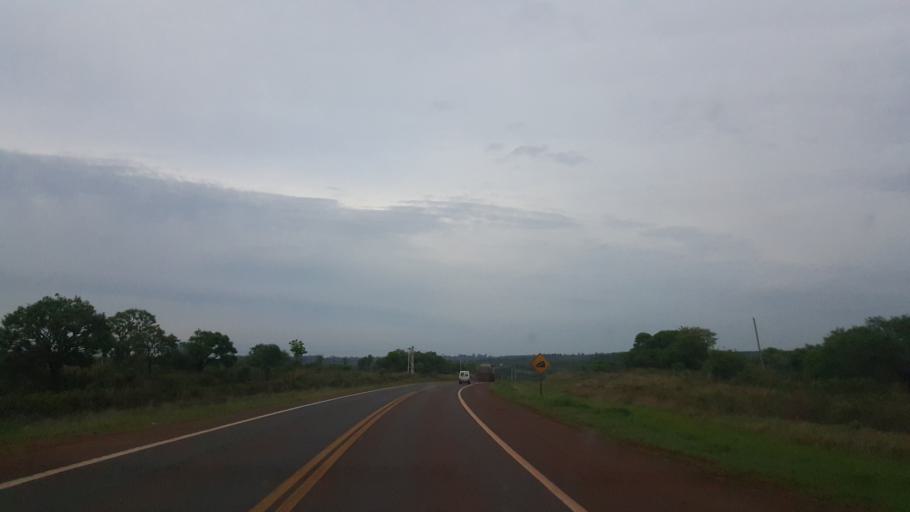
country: AR
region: Misiones
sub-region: Departamento de Apostoles
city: San Jose
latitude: -27.7602
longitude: -55.7899
